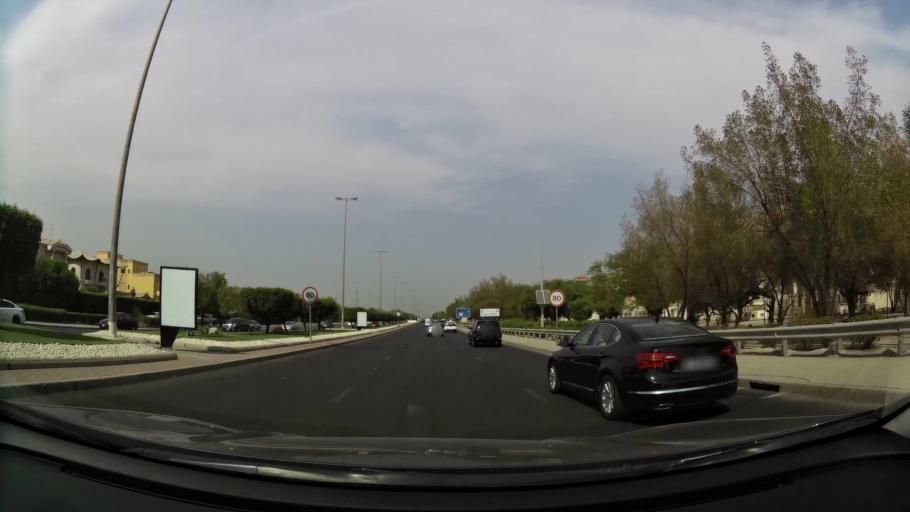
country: KW
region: Muhafazat Hawalli
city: Hawalli
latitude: 29.3081
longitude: 47.9986
